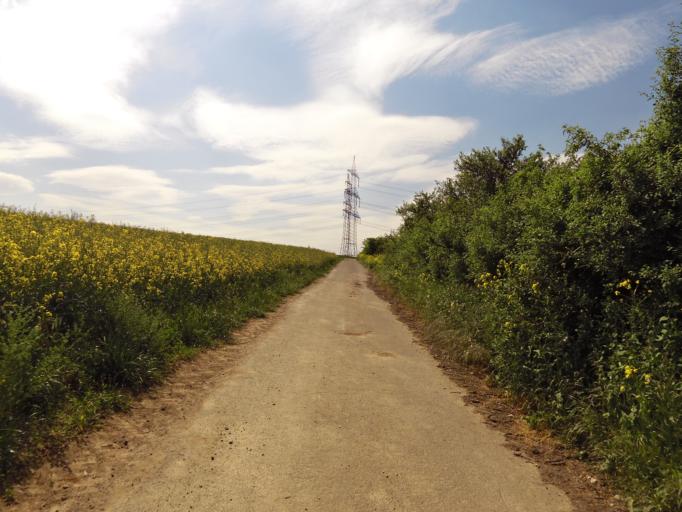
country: DE
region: Rheinland-Pfalz
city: Kerzenheim
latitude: 49.5852
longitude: 8.0609
